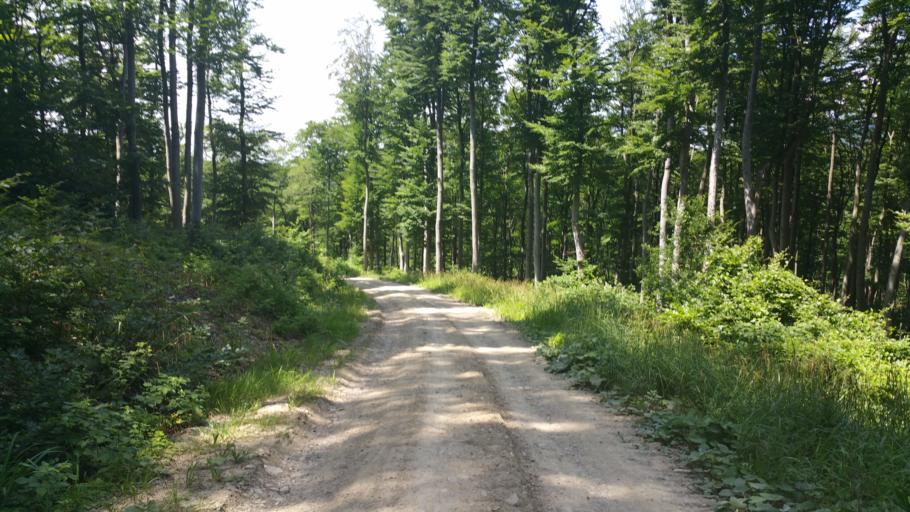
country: AT
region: Lower Austria
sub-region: Politischer Bezirk Wien-Umgebung
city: Klosterneuburg
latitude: 48.2361
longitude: 16.2733
